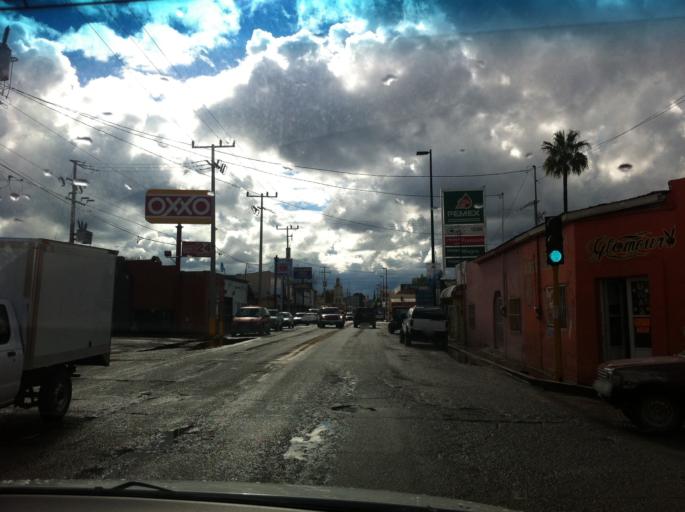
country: MX
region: Sonora
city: Magdalena de Kino
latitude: 30.6272
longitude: -110.9674
